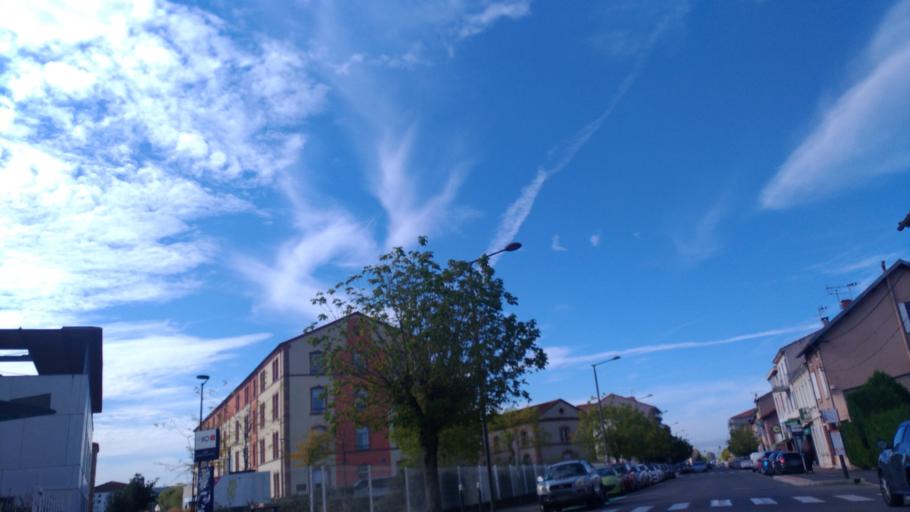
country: FR
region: Midi-Pyrenees
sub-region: Departement du Tarn
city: Albi
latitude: 43.9199
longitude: 2.1389
